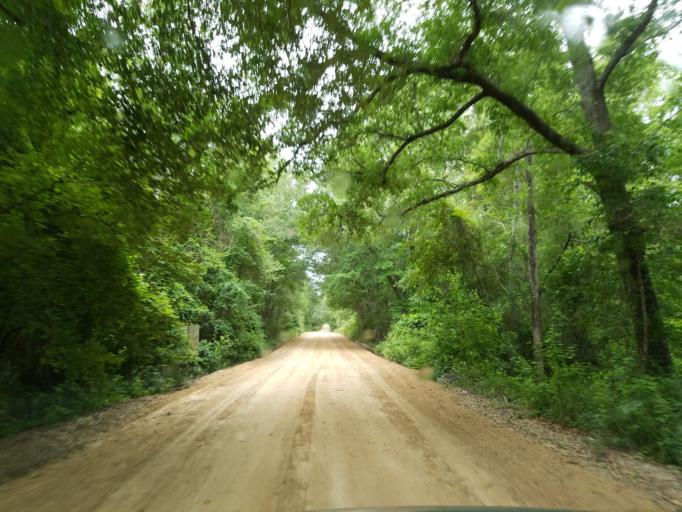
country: US
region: Georgia
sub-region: Crisp County
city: Cordele
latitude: 32.0208
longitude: -83.7213
